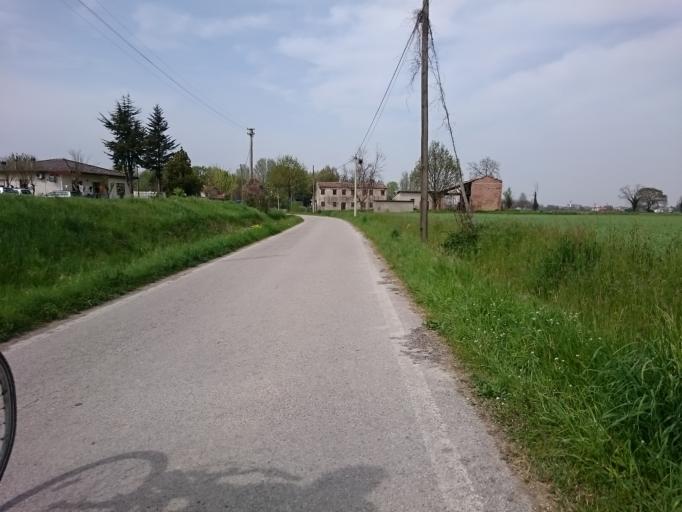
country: IT
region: Veneto
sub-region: Provincia di Padova
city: Tribano
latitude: 45.1916
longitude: 11.8293
